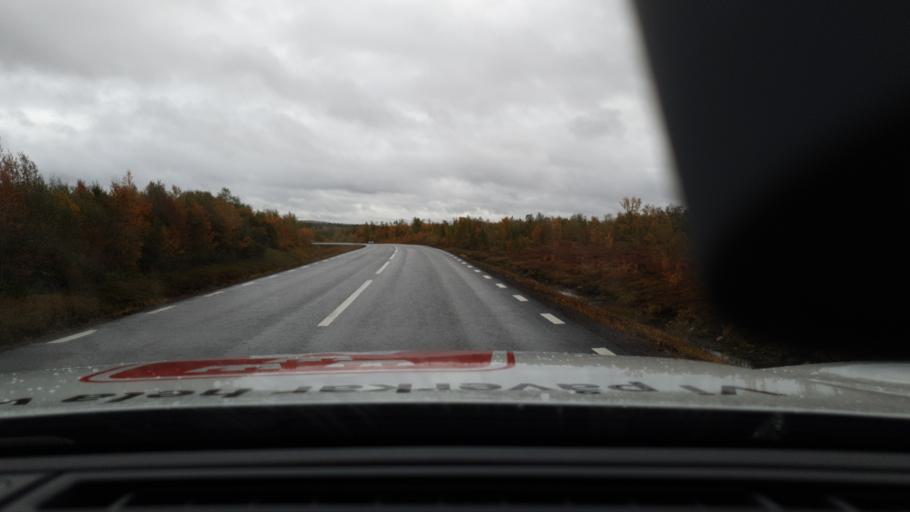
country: SE
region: Norrbotten
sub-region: Kiruna Kommun
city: Kiruna
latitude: 67.9968
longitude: 19.8710
